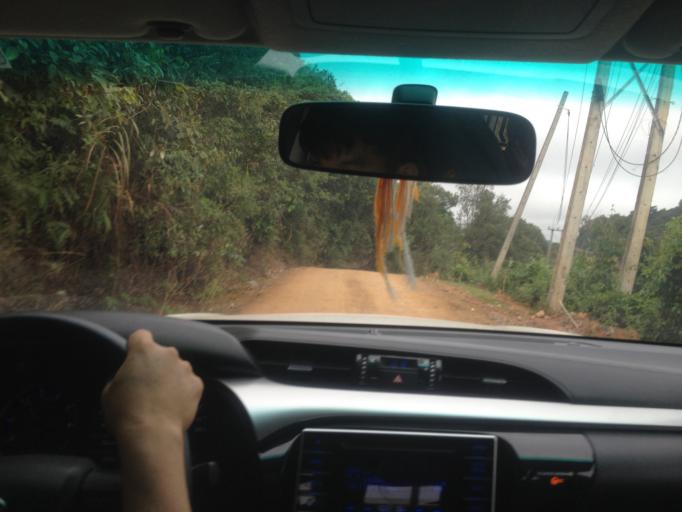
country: TH
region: Nan
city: Chaloem Phra Kiat
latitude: 19.9696
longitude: 101.1366
